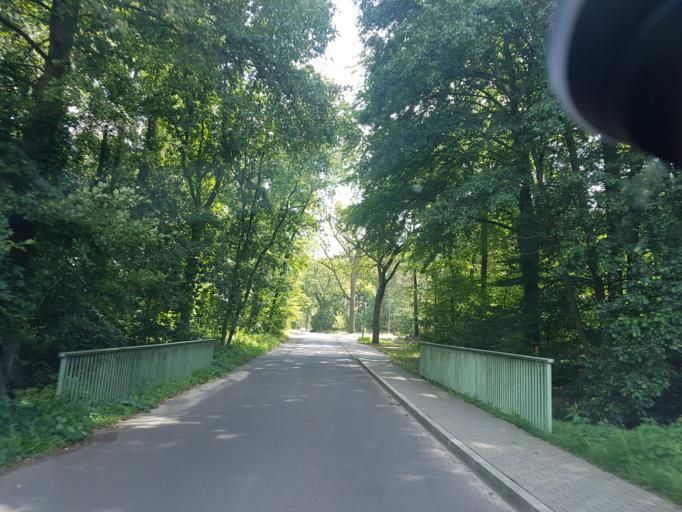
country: DE
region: Brandenburg
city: Gross Kreutz
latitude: 52.3172
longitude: 12.7707
